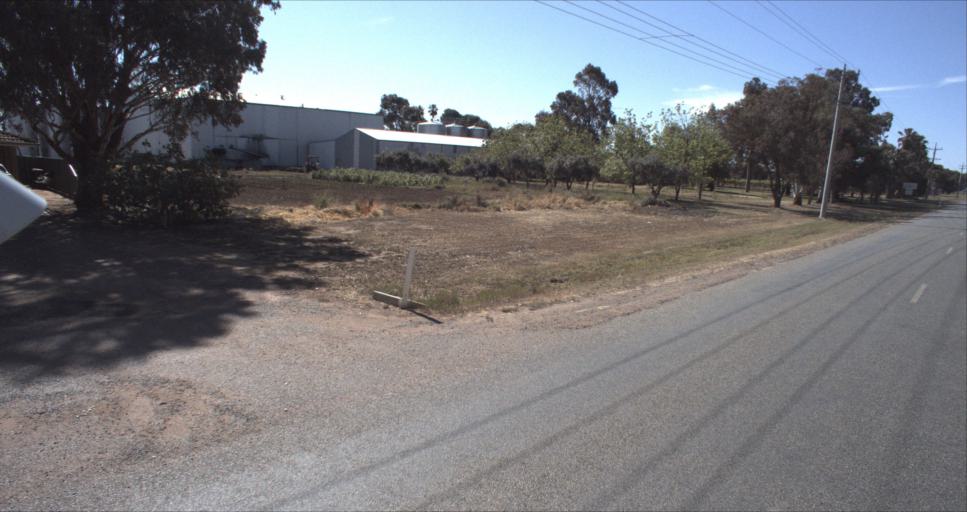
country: AU
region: New South Wales
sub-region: Leeton
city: Leeton
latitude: -34.5583
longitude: 146.3841
